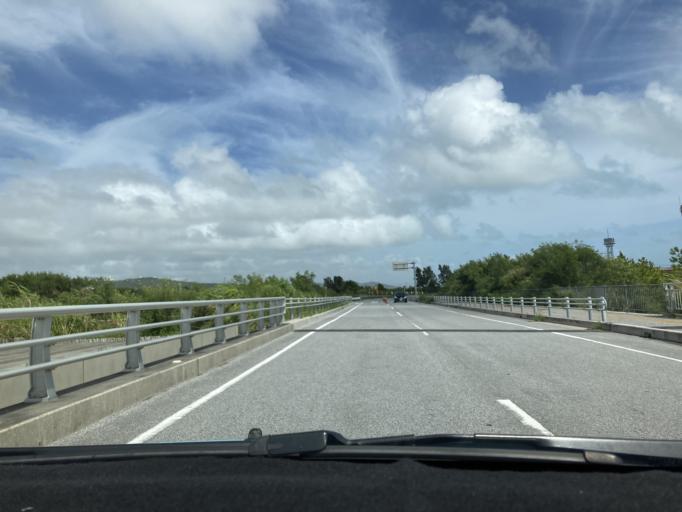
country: JP
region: Okinawa
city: Ginowan
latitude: 26.2162
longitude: 127.7723
